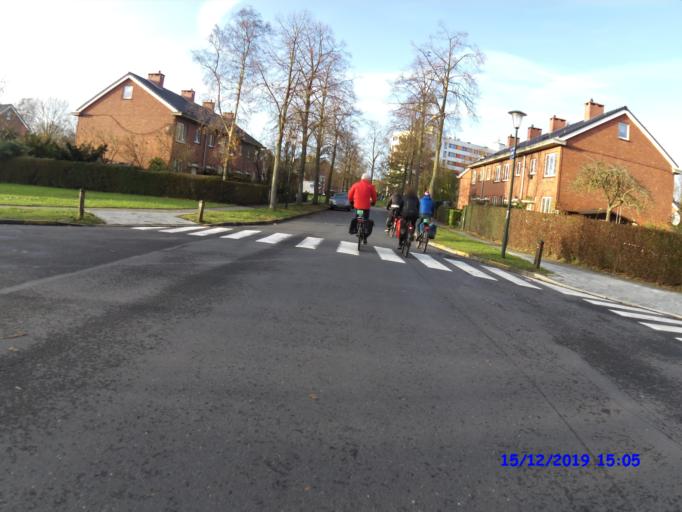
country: BE
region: Flanders
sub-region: Provincie Vlaams-Brabant
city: Drogenbos
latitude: 50.7880
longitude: 4.3252
